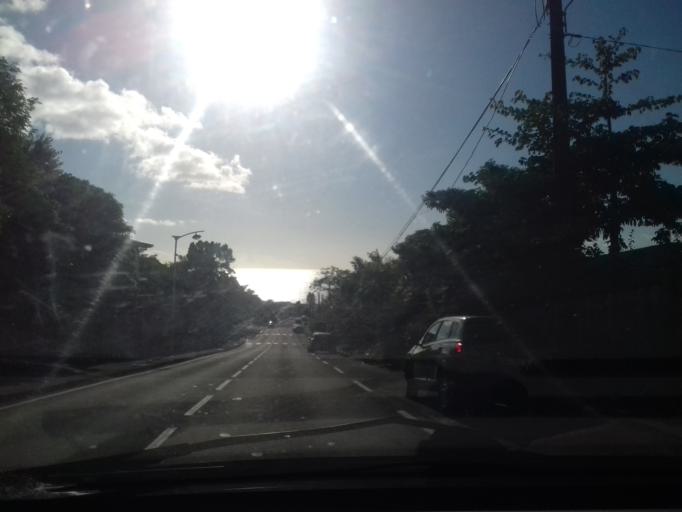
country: MQ
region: Martinique
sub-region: Martinique
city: Fort-de-France
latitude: 14.6175
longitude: -61.0973
